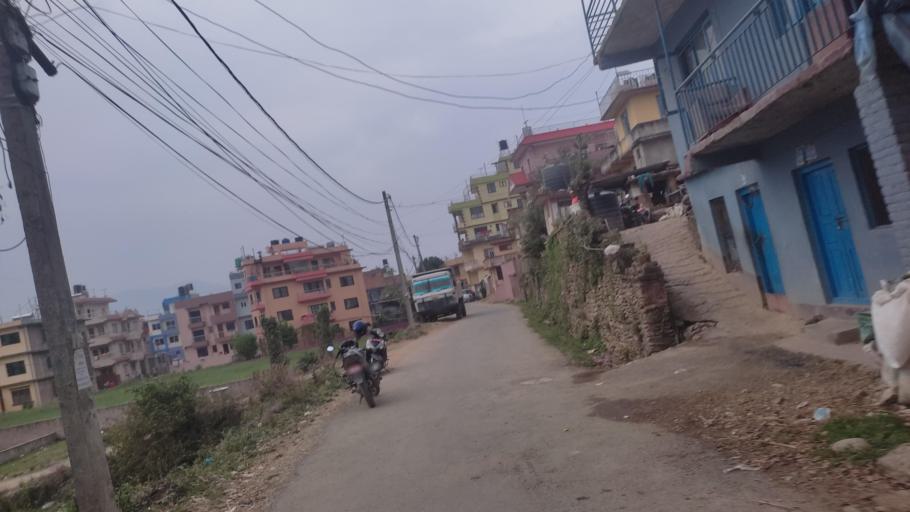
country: NP
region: Central Region
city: Kirtipur
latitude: 27.6661
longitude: 85.2864
